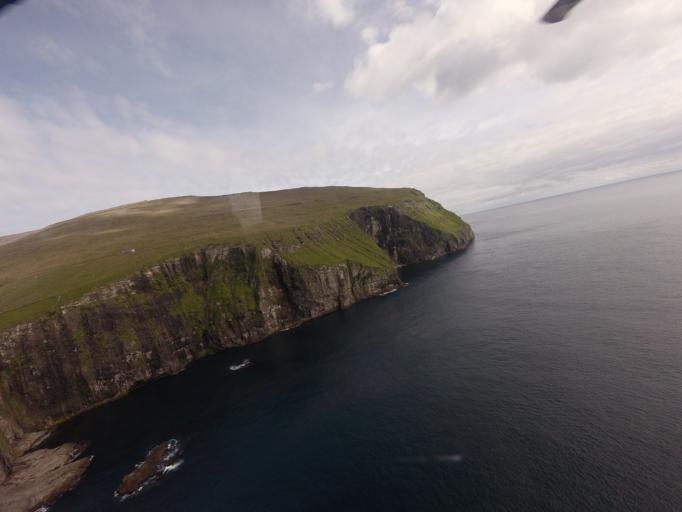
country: FO
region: Nordoyar
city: Klaksvik
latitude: 62.3148
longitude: -6.3084
